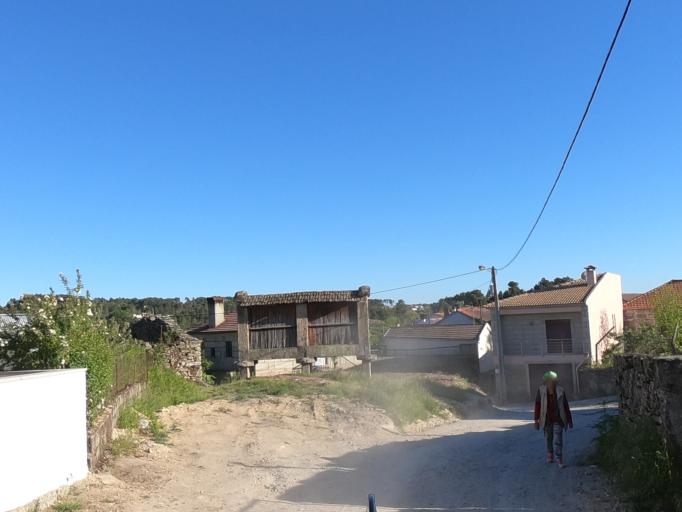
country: PT
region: Vila Real
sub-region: Vila Real
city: Vila Real
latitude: 41.3290
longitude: -7.6920
